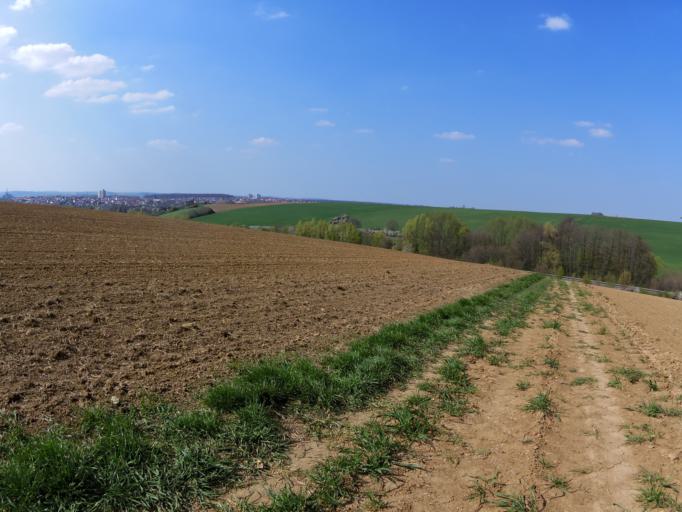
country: DE
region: Bavaria
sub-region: Regierungsbezirk Unterfranken
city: Rottendorf
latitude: 49.7808
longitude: 10.0463
